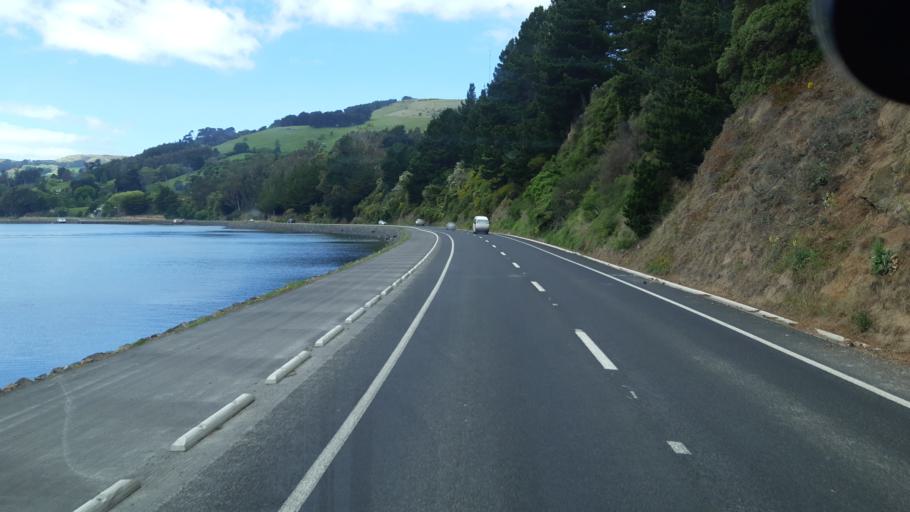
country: NZ
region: Otago
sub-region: Dunedin City
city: Dunedin
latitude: -45.8792
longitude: 170.5668
